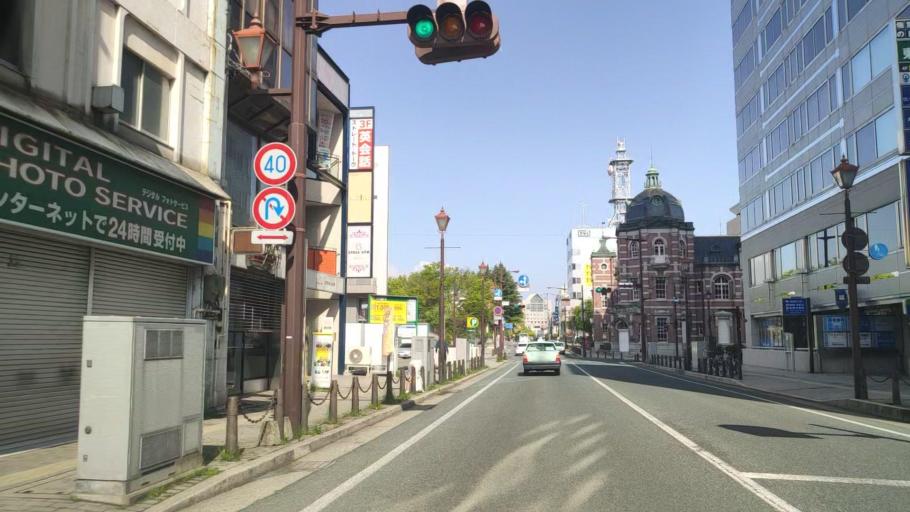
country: JP
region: Iwate
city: Morioka-shi
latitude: 39.7000
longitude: 141.1559
